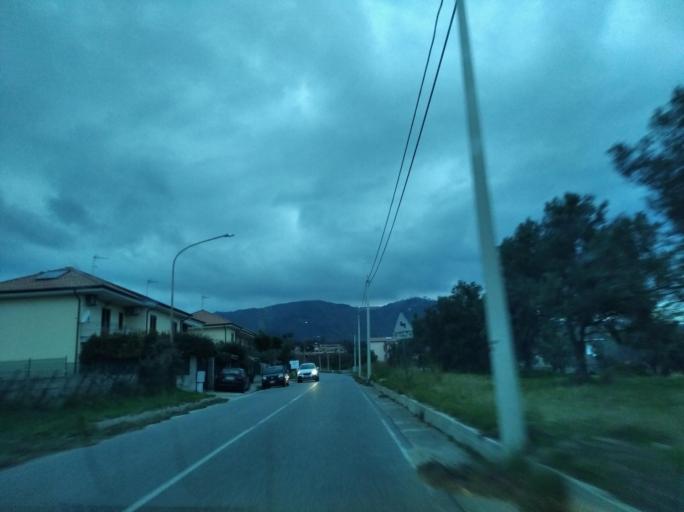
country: IT
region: Calabria
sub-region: Provincia di Catanzaro
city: Soverato Superiore
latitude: 38.7094
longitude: 16.5257
